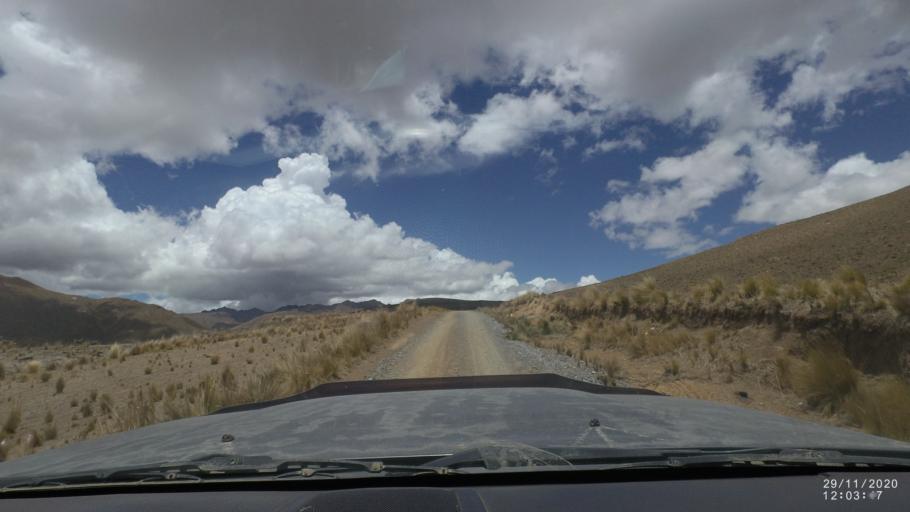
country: BO
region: Cochabamba
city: Cochabamba
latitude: -17.1495
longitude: -66.2870
